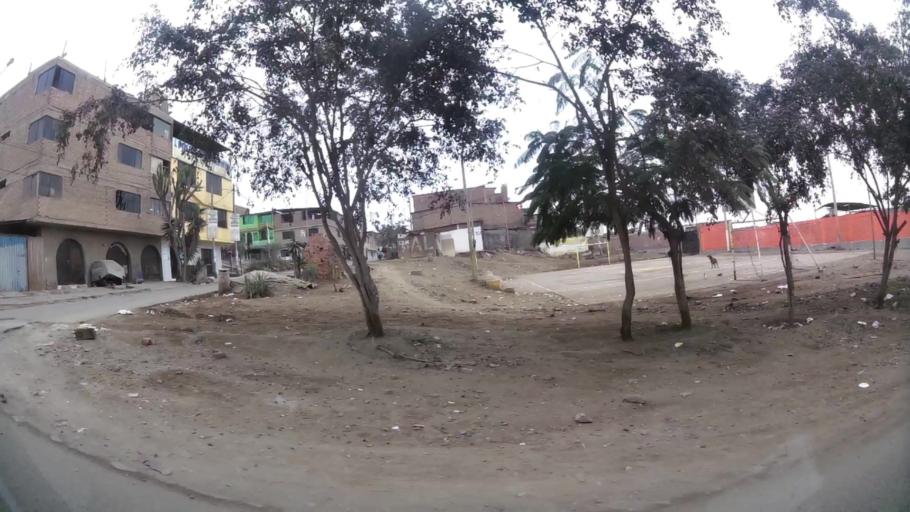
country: PE
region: Lima
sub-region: Lima
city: Surco
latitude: -12.1638
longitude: -76.9588
